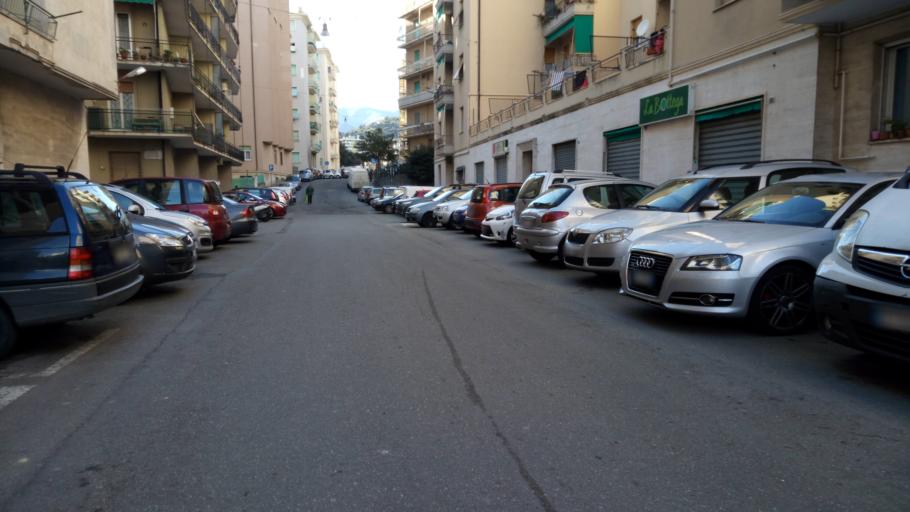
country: IT
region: Liguria
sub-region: Provincia di Genova
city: Mele
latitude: 44.4292
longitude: 8.7727
